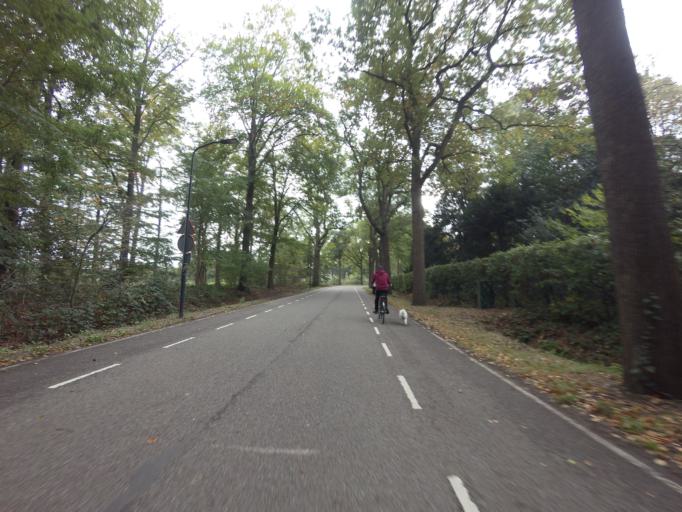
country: NL
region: North Brabant
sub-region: Gemeente Breda
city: Breda
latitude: 51.5637
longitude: 4.7515
